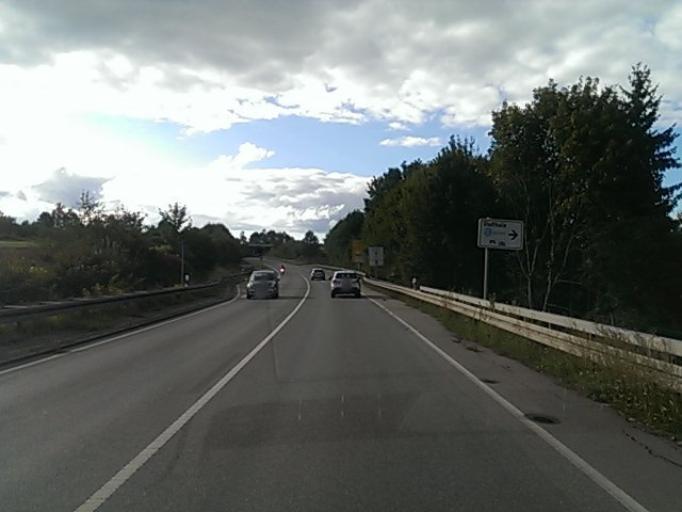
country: DE
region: Baden-Wuerttemberg
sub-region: Freiburg Region
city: Rottweil
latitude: 48.1477
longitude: 8.6306
